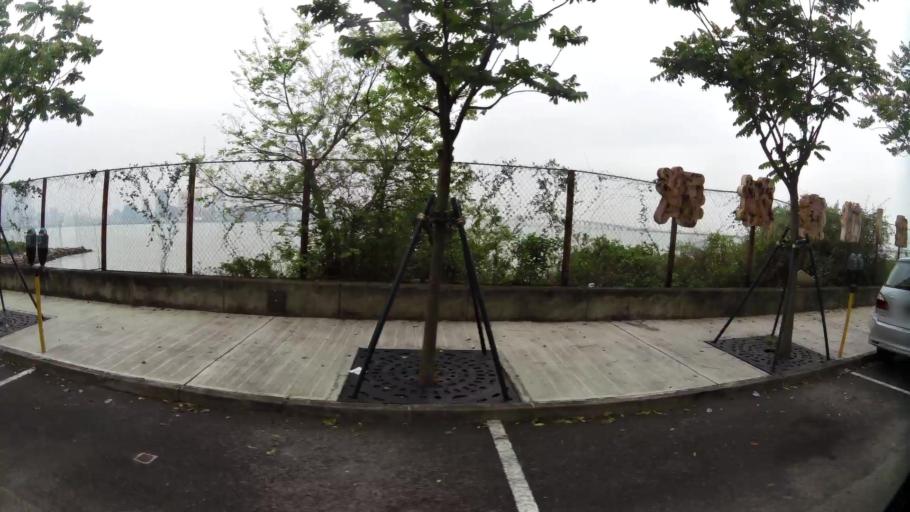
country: MO
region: Macau
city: Macau
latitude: 22.1659
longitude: 113.5575
